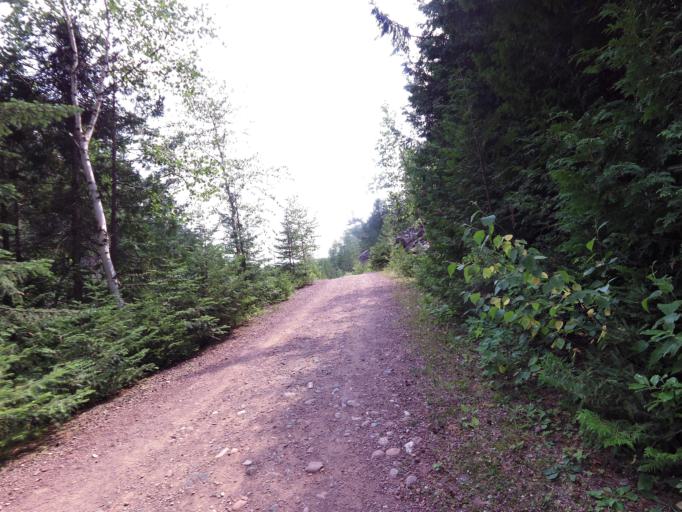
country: CA
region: Ontario
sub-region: Thunder Bay District
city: Thunder Bay
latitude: 48.7987
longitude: -88.6188
